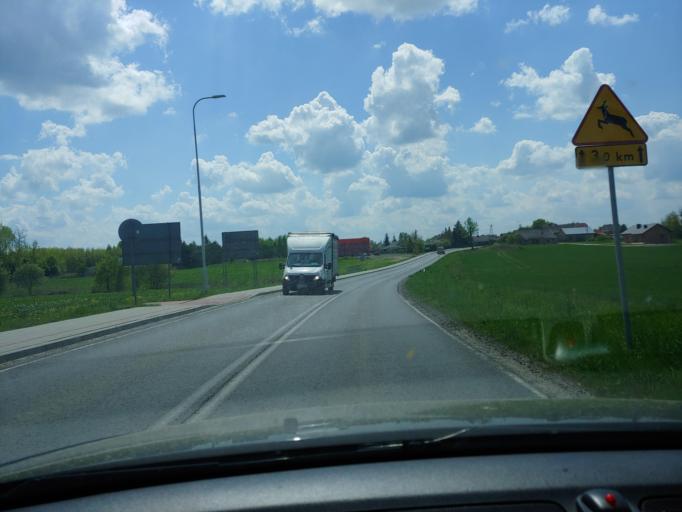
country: PL
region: Subcarpathian Voivodeship
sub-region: Powiat mielecki
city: Radomysl Wielki
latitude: 50.1861
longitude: 21.2637
